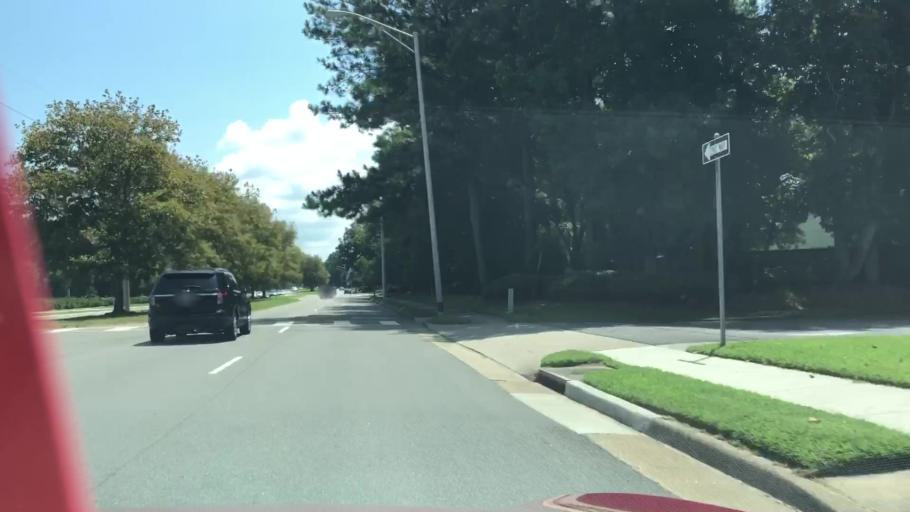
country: US
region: Virginia
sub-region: City of Virginia Beach
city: Virginia Beach
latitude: 36.8964
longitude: -76.0621
